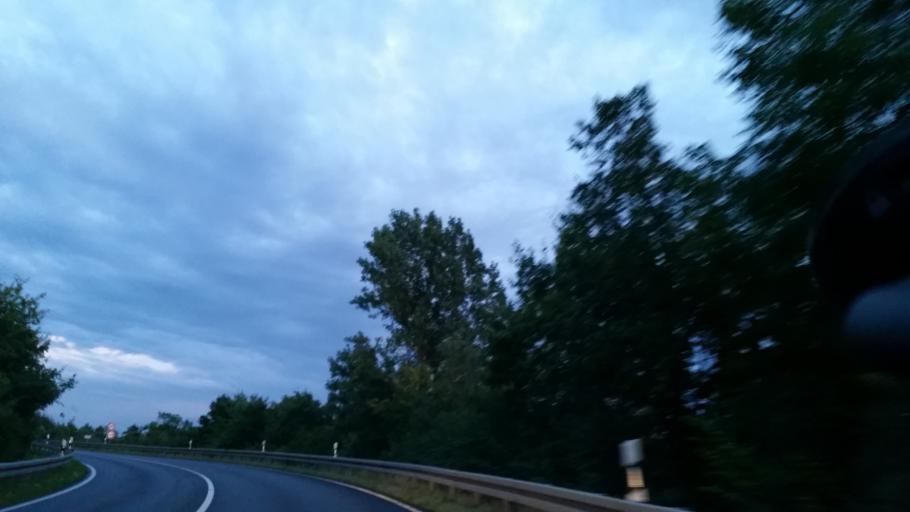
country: DE
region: Lower Saxony
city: Braunschweig
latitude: 52.2991
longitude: 10.4774
